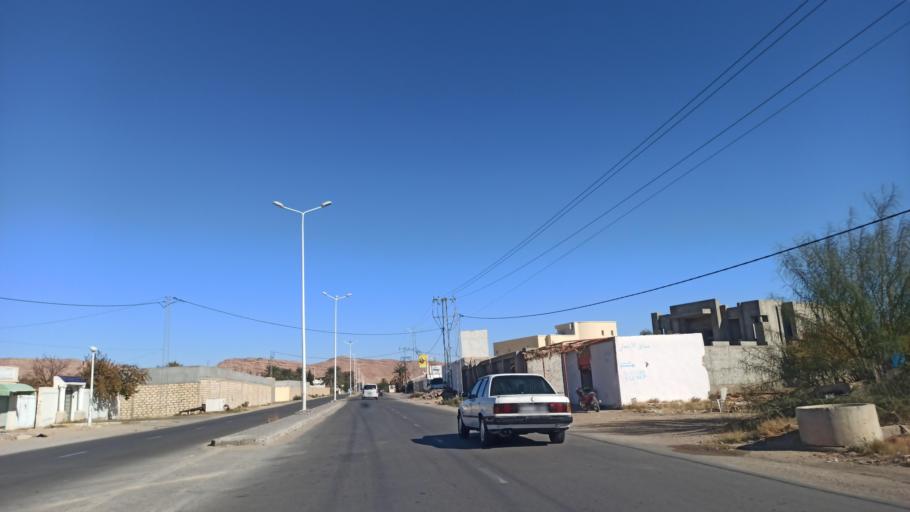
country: TN
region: Gafsa
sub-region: Gafsa Municipality
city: Gafsa
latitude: 34.4102
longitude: 8.7369
